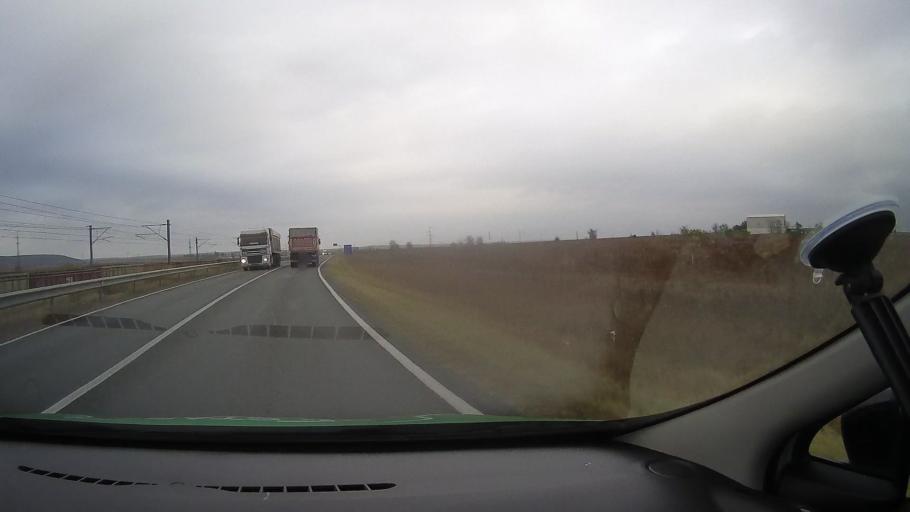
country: RO
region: Constanta
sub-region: Comuna Poarta Alba
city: Poarta Alba
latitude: 44.2300
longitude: 28.3786
